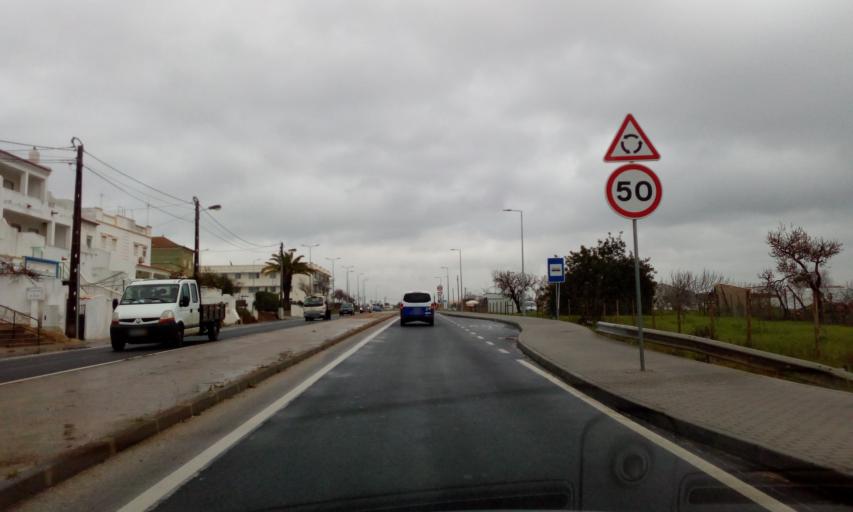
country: PT
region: Faro
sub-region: Lagos
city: Lagos
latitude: 37.1304
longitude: -8.6684
